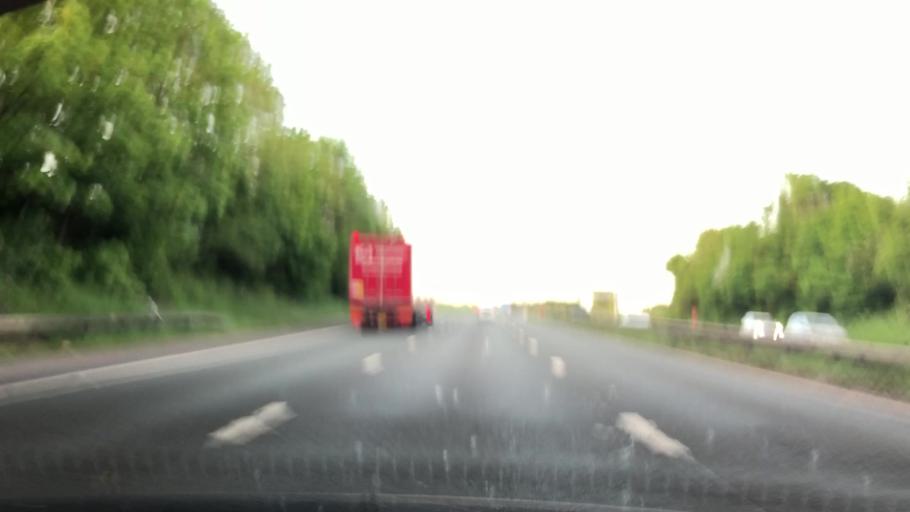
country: GB
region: England
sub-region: Cheshire West and Chester
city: Elton
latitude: 53.2588
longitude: -2.8258
